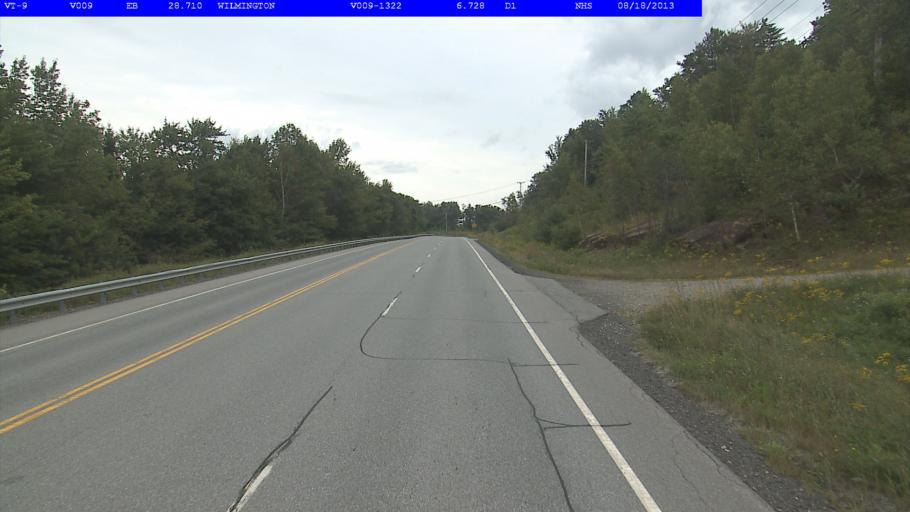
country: US
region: Vermont
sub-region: Windham County
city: Dover
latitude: 42.8571
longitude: -72.8089
